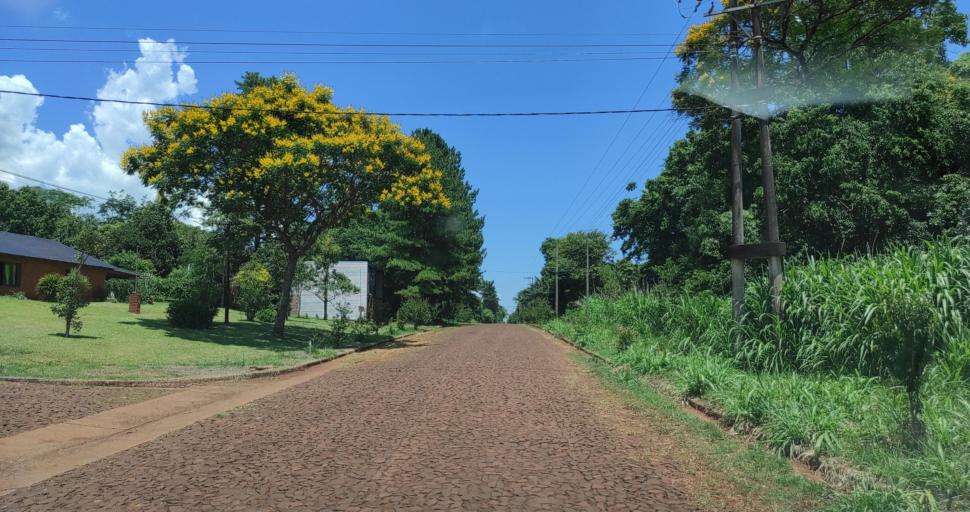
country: AR
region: Misiones
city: Ruiz de Montoya
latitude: -26.9687
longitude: -55.0496
